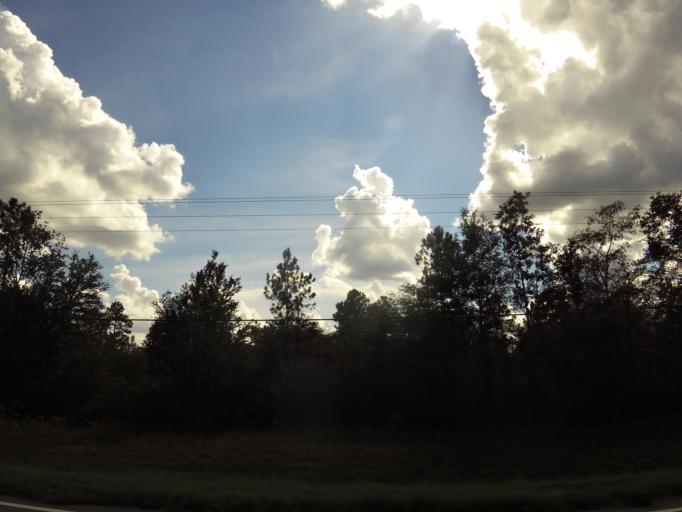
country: US
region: Georgia
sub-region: Echols County
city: Statenville
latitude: 30.7745
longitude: -83.1467
